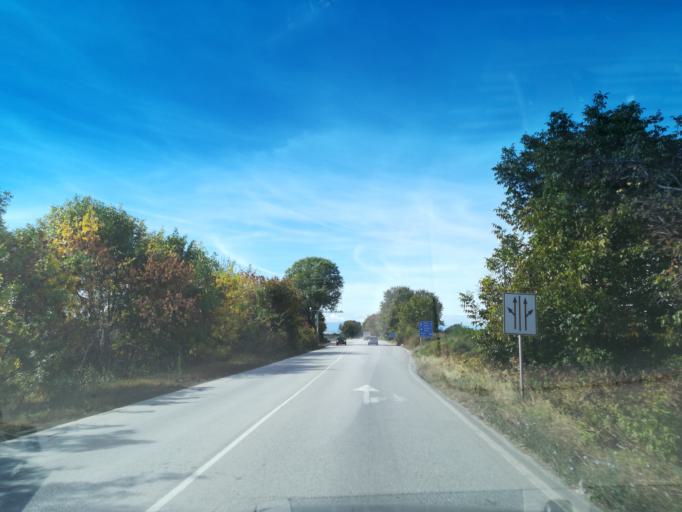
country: BG
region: Plovdiv
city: Stamboliyski
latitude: 42.1355
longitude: 24.6370
